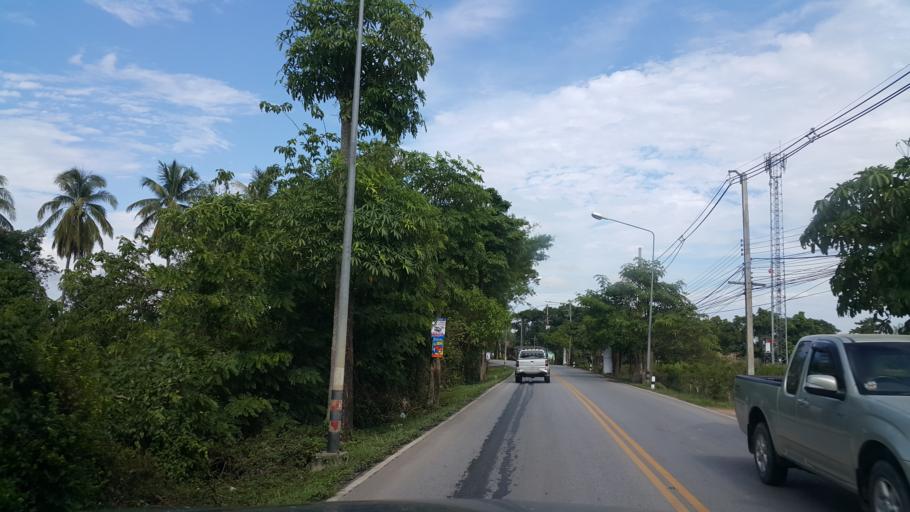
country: TH
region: Chiang Rai
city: Chiang Rai
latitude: 19.9130
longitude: 99.8711
